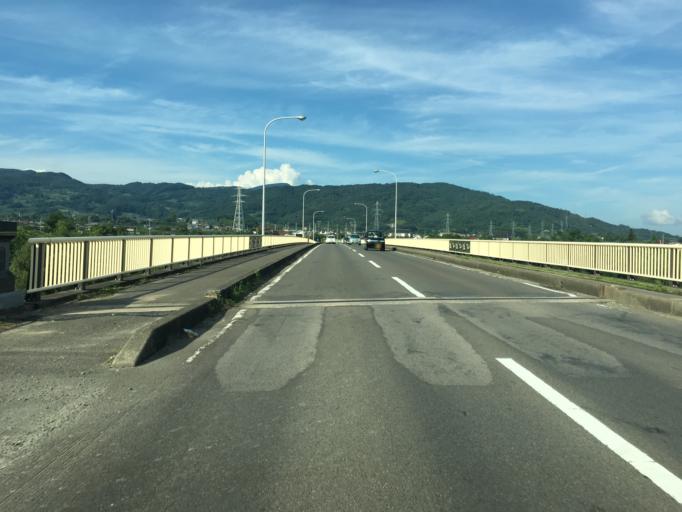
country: JP
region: Fukushima
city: Fukushima-shi
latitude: 37.8175
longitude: 140.4647
